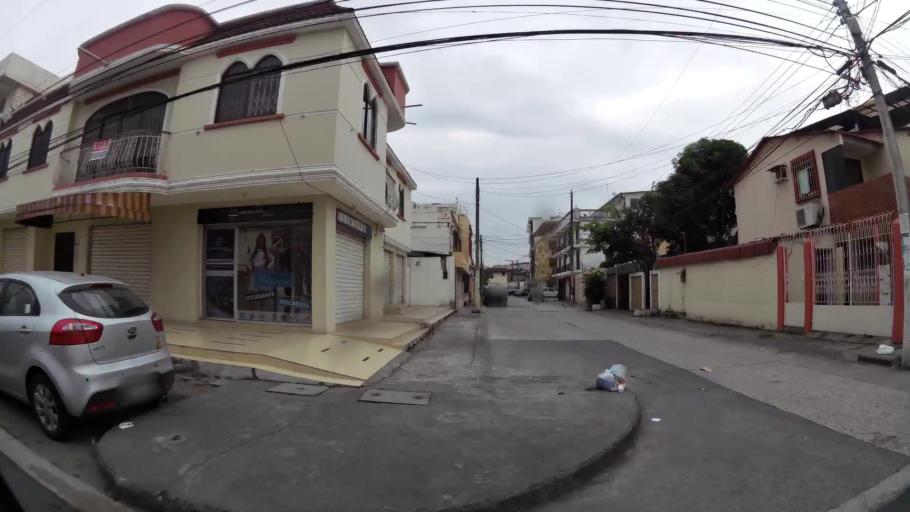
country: EC
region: Guayas
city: Eloy Alfaro
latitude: -2.1395
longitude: -79.9063
